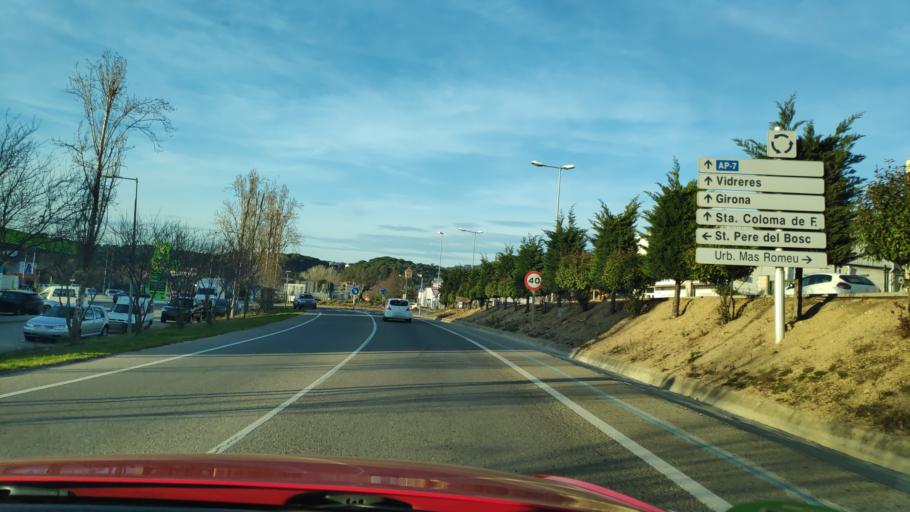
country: ES
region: Catalonia
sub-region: Provincia de Girona
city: Lloret de Mar
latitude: 41.7132
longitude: 2.8315
